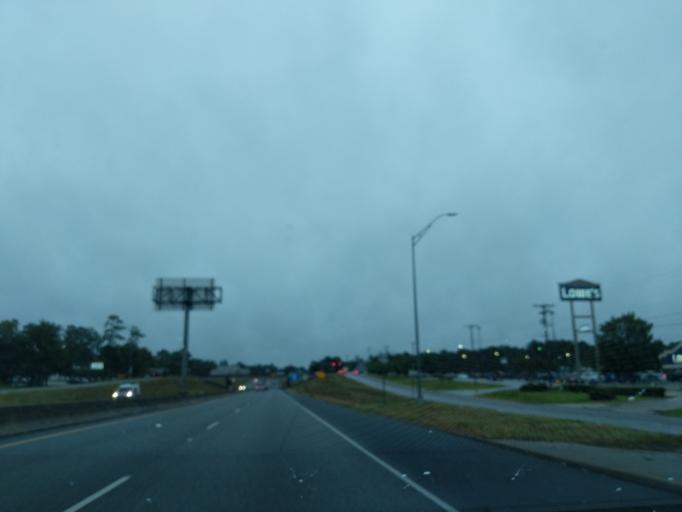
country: US
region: Texas
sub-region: Angelina County
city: Lufkin
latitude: 31.3147
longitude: -94.7135
